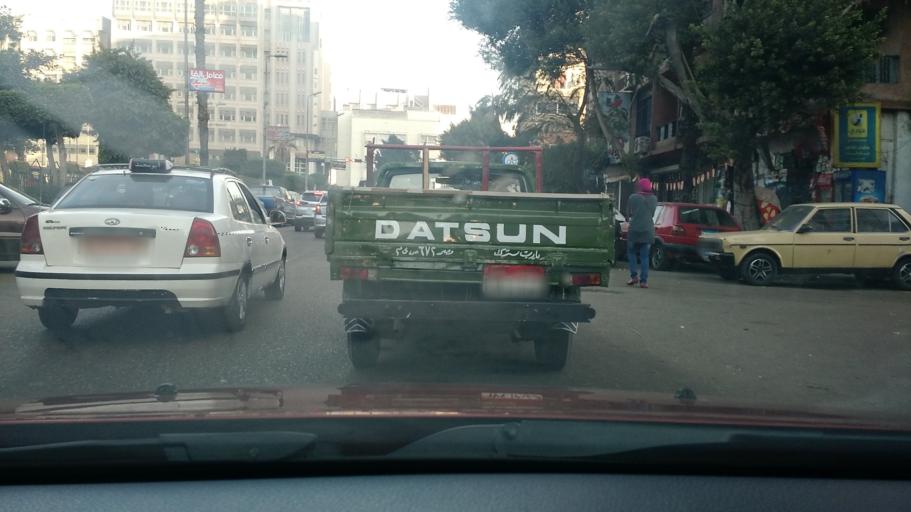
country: EG
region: Al Jizah
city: Al Jizah
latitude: 30.0272
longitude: 31.2272
